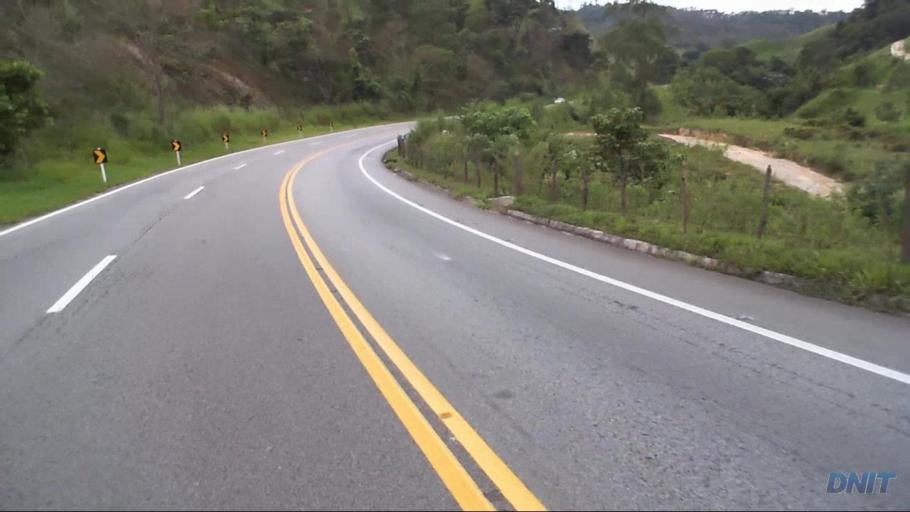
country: BR
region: Minas Gerais
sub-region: Nova Era
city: Nova Era
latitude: -19.6287
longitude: -42.8734
